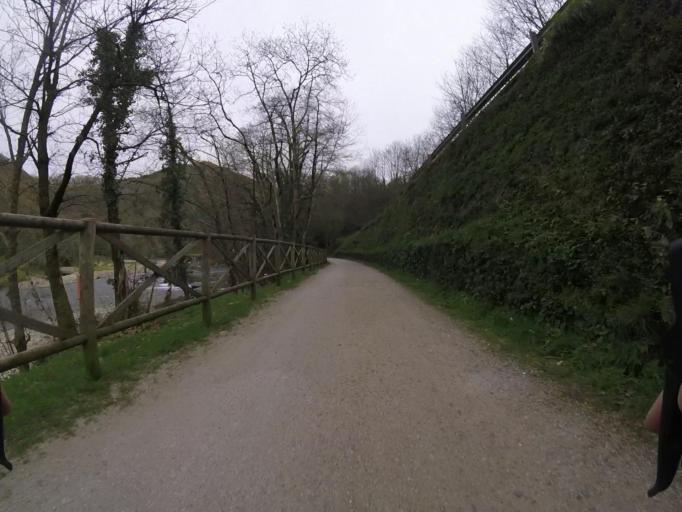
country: ES
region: Basque Country
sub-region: Provincia de Guipuzcoa
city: Irun
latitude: 43.3107
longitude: -1.7400
